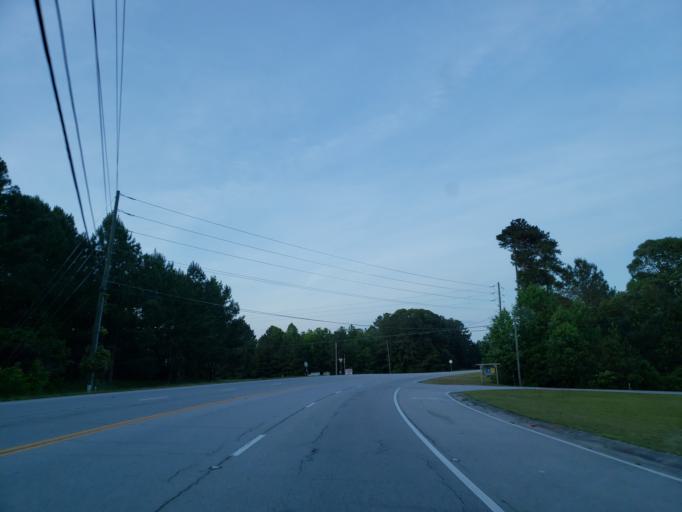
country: US
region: Georgia
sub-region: Fulton County
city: Chattahoochee Hills
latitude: 33.6435
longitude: -84.8312
